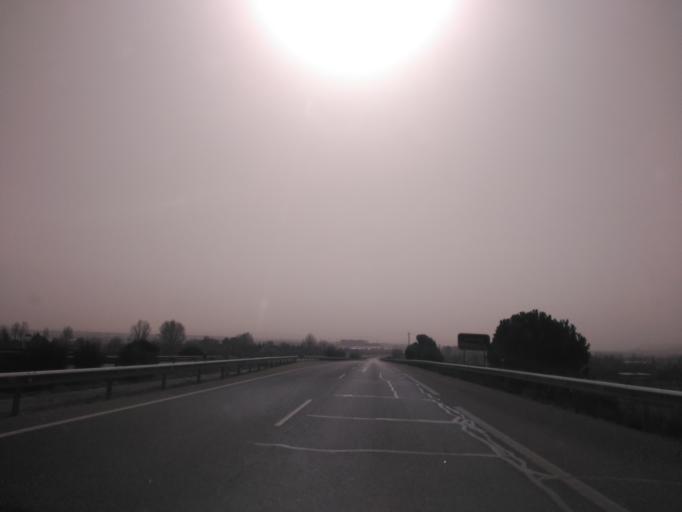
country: ES
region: Castille and Leon
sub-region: Provincia de Palencia
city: Villamuriel de Cerrato
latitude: 41.9805
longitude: -4.5015
